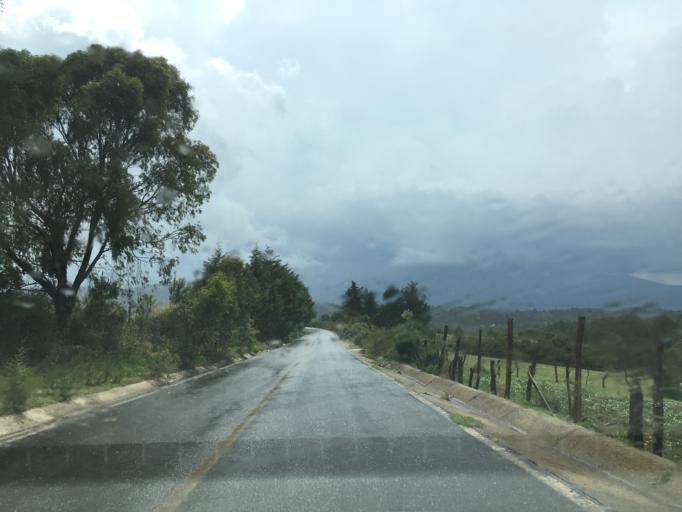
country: MX
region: Michoacan
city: Acuitzio del Canje
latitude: 19.5284
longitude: -101.2386
